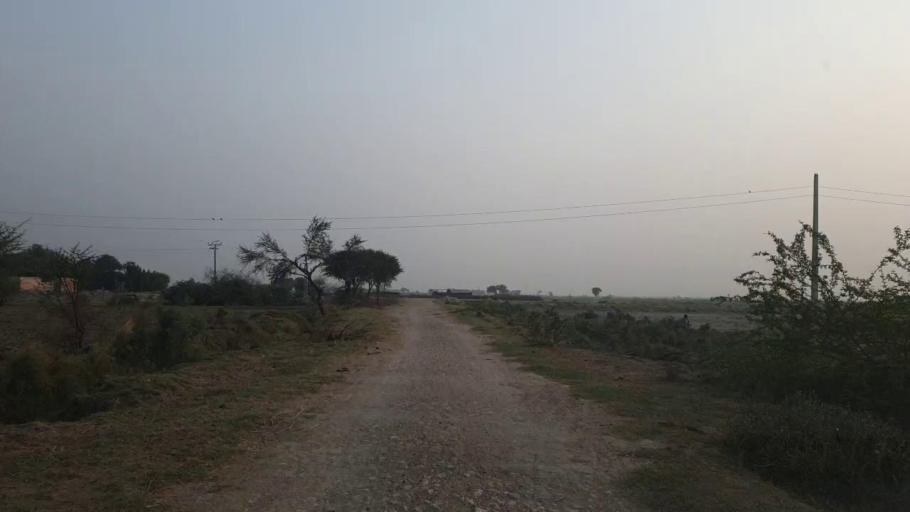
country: PK
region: Sindh
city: Mirpur Batoro
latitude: 24.6617
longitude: 68.3748
